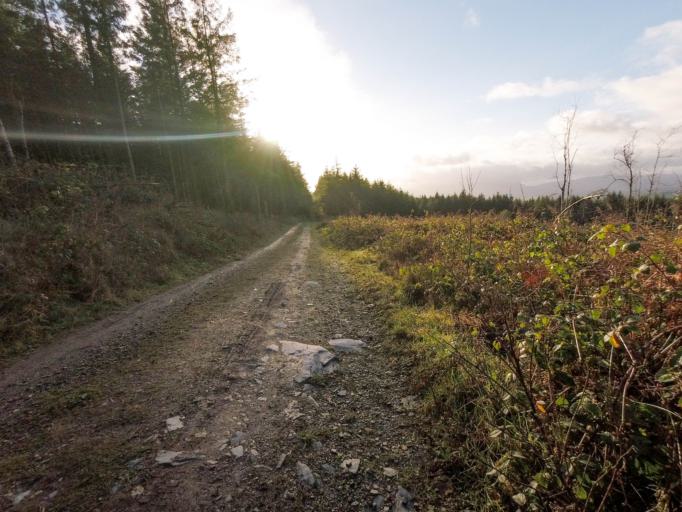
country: IE
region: Munster
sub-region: Waterford
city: Portlaw
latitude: 52.3122
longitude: -7.3505
